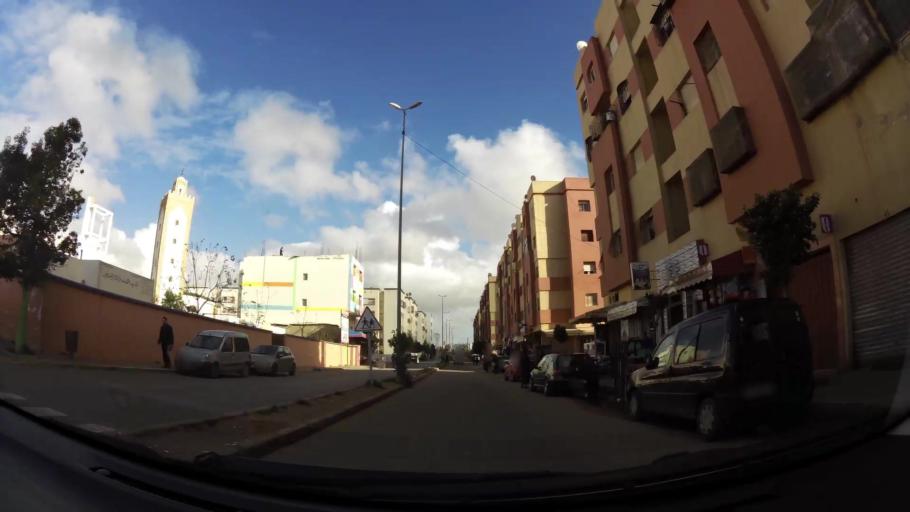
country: MA
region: Grand Casablanca
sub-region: Casablanca
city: Casablanca
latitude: 33.5491
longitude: -7.7043
